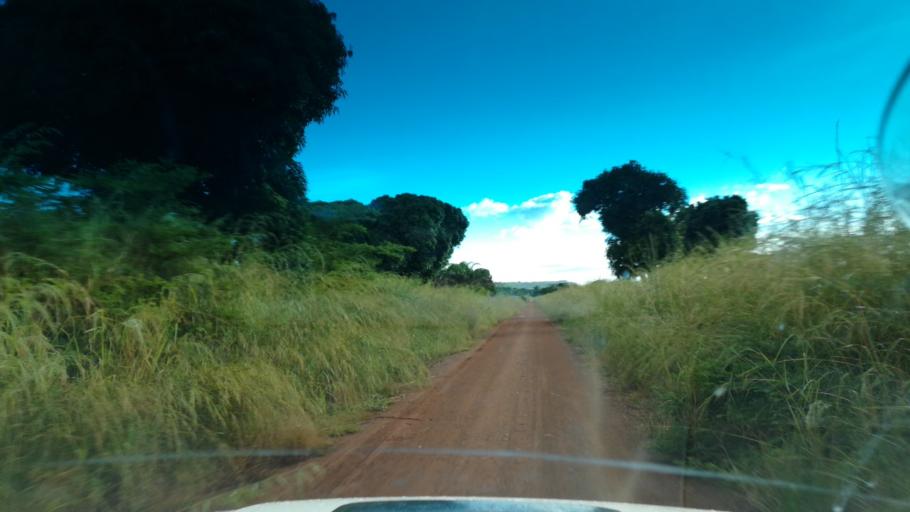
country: ZM
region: Northern
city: Kaputa
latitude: -8.4015
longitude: 28.9401
